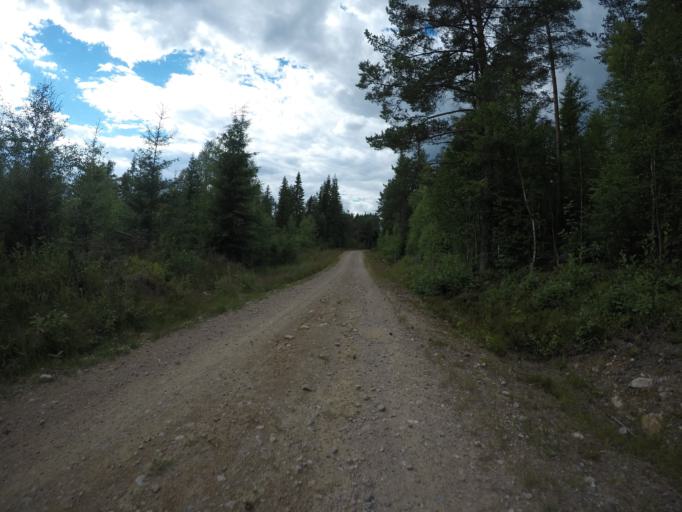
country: SE
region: Vaermland
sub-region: Filipstads Kommun
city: Lesjofors
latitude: 60.0706
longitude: 14.4561
